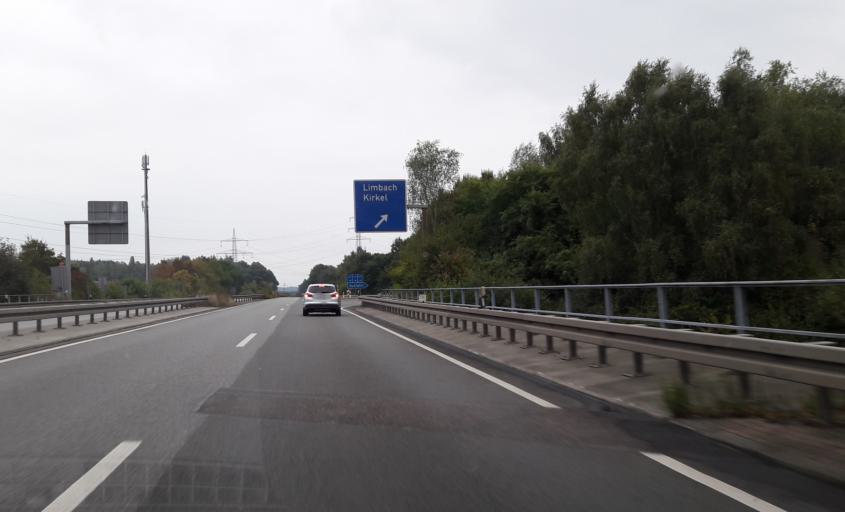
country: DE
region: Saarland
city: Kirkel
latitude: 49.3056
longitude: 7.2672
